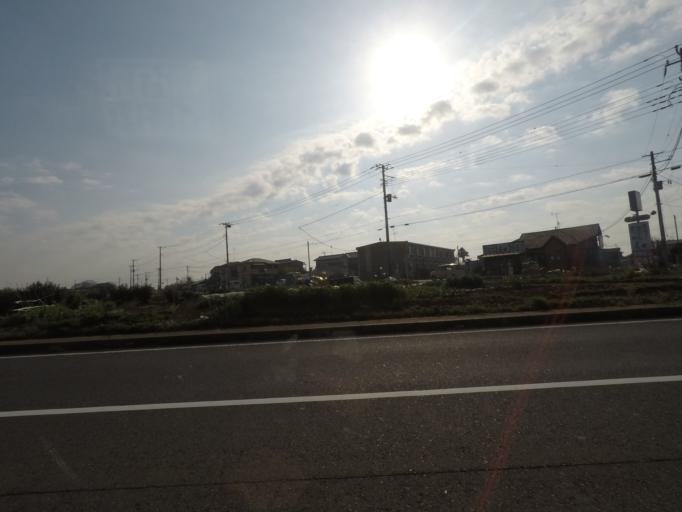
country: JP
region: Chiba
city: Narita
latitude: 35.7332
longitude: 140.3157
